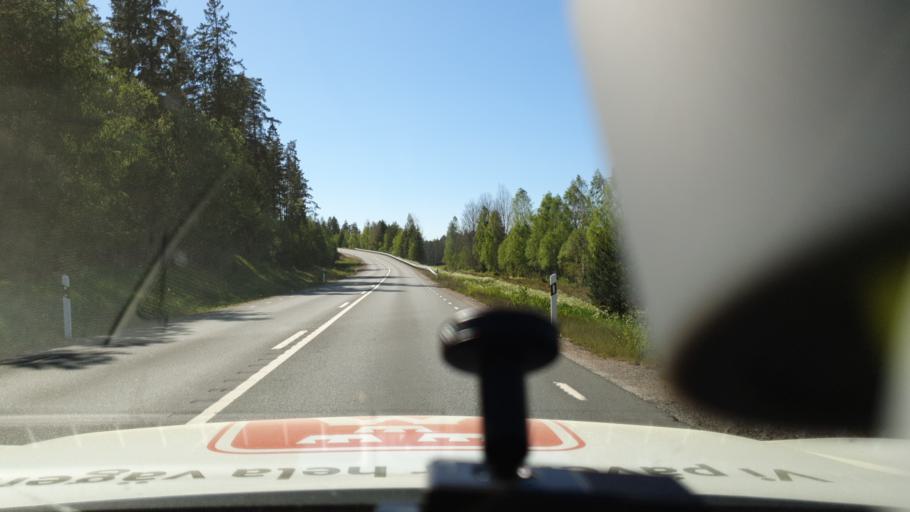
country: SE
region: Kronoberg
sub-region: Uppvidinge Kommun
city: Aseda
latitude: 57.3979
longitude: 15.3608
